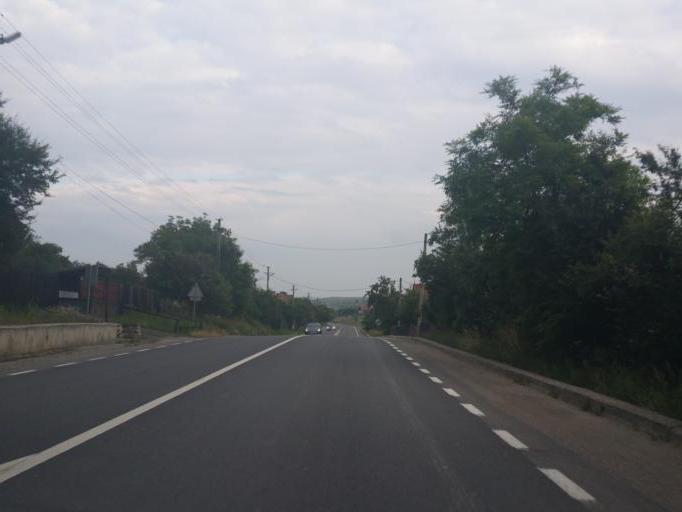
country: RO
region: Cluj
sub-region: Comuna Sanpaul
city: Sanpaul
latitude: 46.9375
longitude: 23.3905
